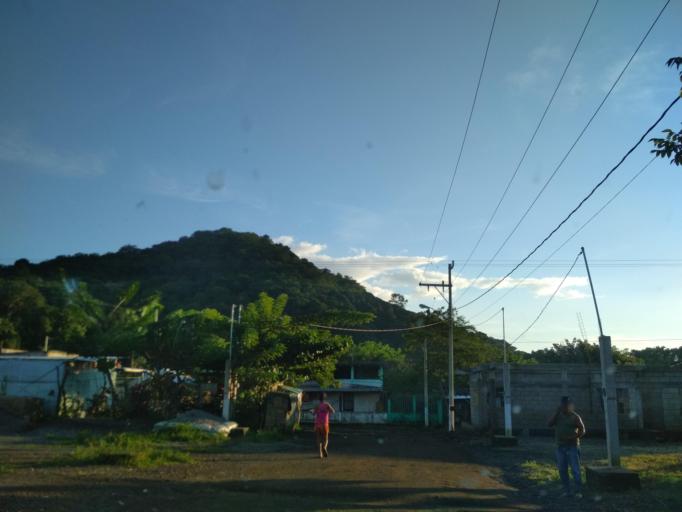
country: MX
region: Veracruz
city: Catemaco
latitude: 18.4209
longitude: -95.1241
